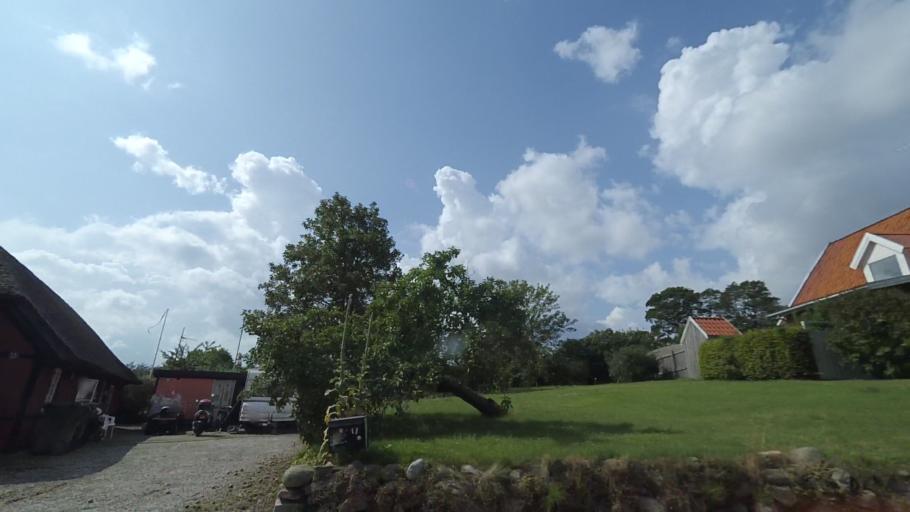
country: DK
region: Central Jutland
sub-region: Norddjurs Kommune
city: Allingabro
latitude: 56.5036
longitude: 10.3333
